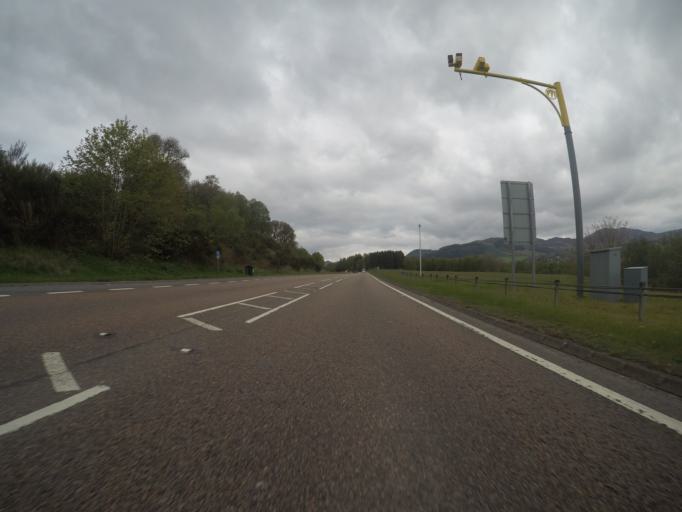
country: GB
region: Scotland
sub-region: Perth and Kinross
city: Pitlochry
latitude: 56.6933
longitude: -3.7278
